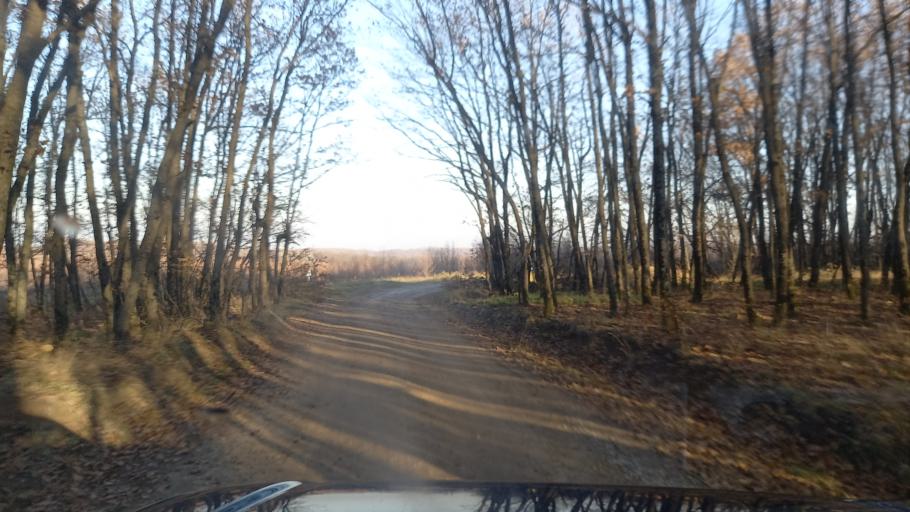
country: RU
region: Krasnodarskiy
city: Azovskaya
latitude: 44.8064
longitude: 38.5911
